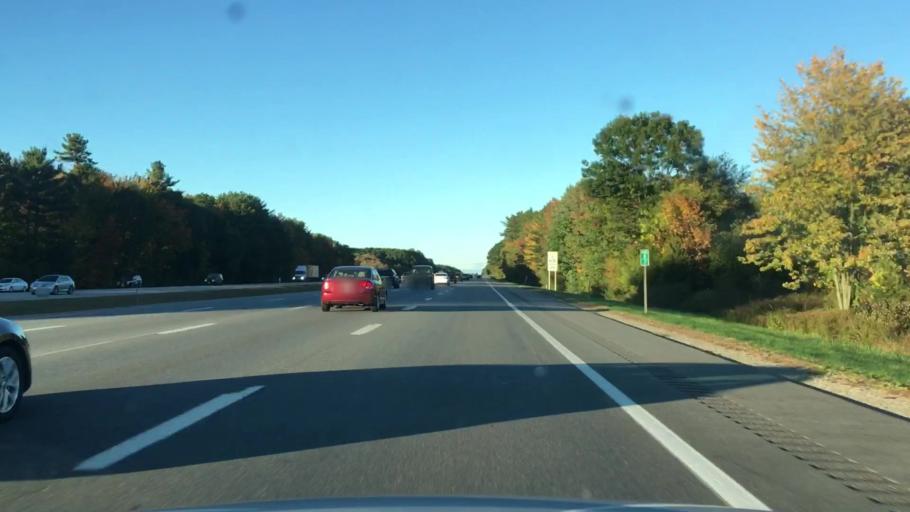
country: US
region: New Hampshire
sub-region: Rockingham County
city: North Hampton
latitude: 42.9962
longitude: -70.8469
